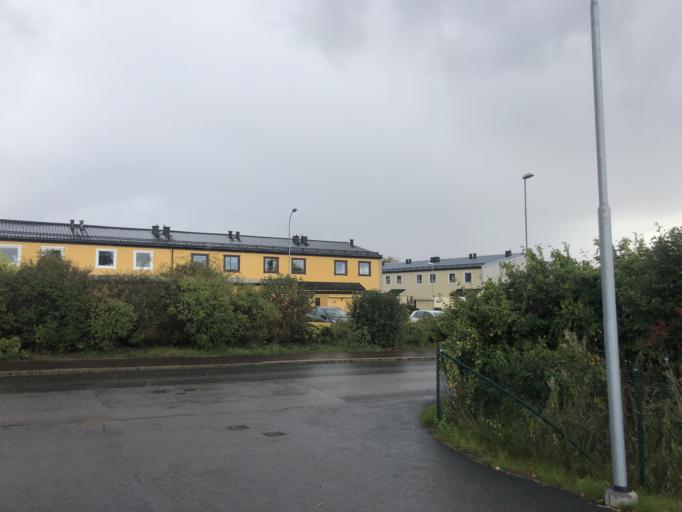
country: SE
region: Vaestra Goetaland
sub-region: Molndal
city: Moelndal
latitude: 57.6504
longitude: 12.0270
